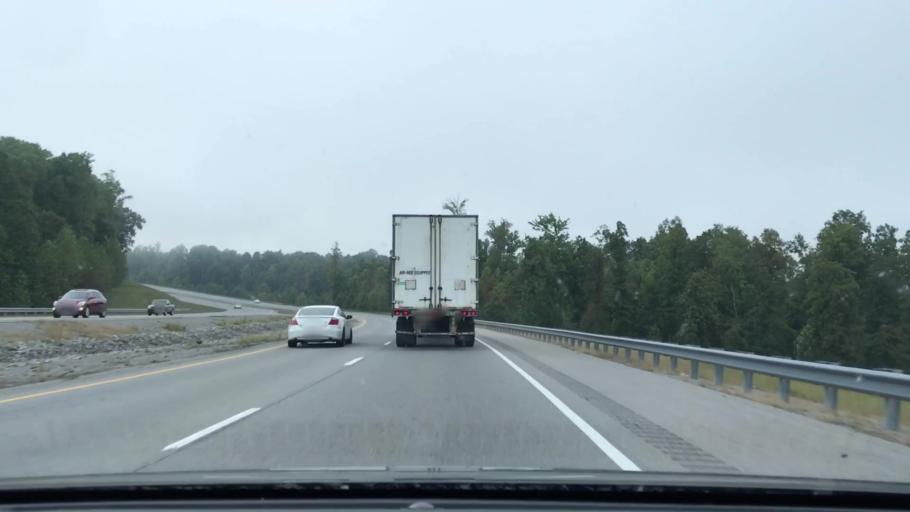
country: US
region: Tennessee
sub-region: Sumner County
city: Gallatin
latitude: 36.4838
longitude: -86.4809
